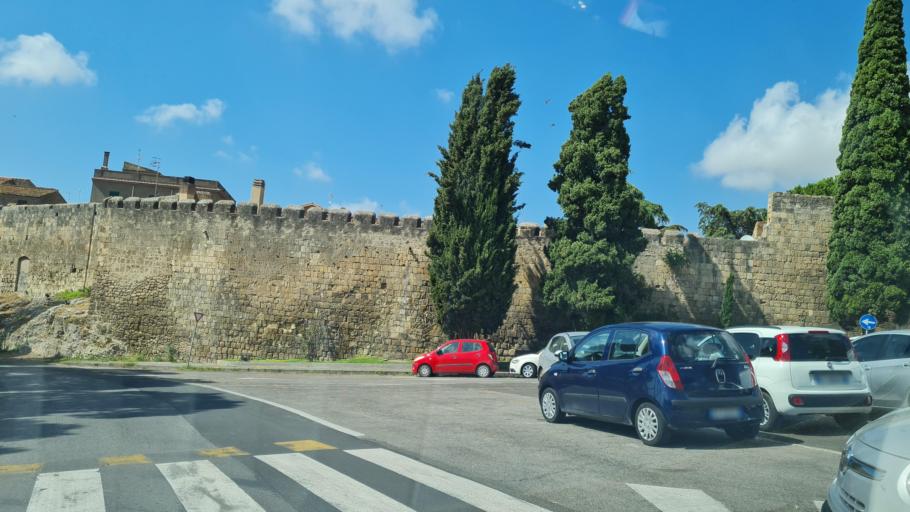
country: IT
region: Latium
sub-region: Provincia di Viterbo
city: Tarquinia
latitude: 42.2507
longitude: 11.7557
